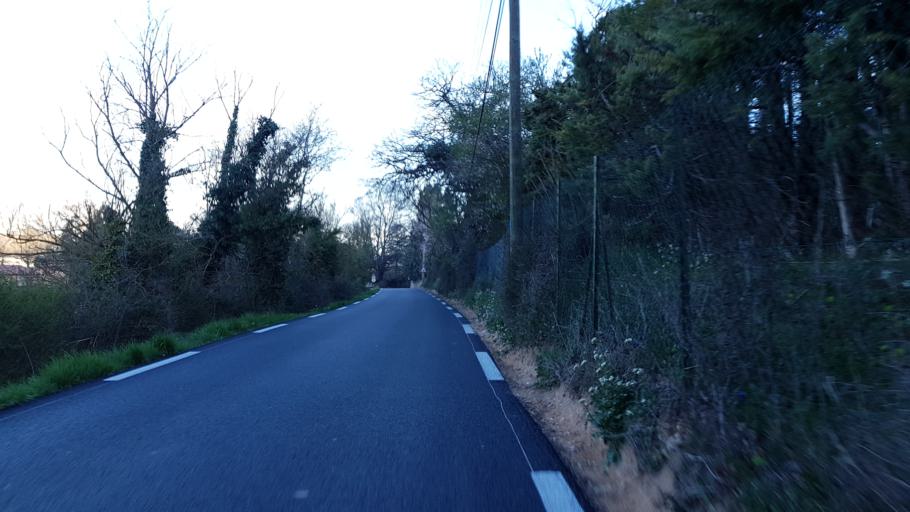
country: FR
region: Provence-Alpes-Cote d'Azur
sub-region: Departement des Bouches-du-Rhone
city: Bouc-Bel-Air
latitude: 43.4944
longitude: 5.4107
